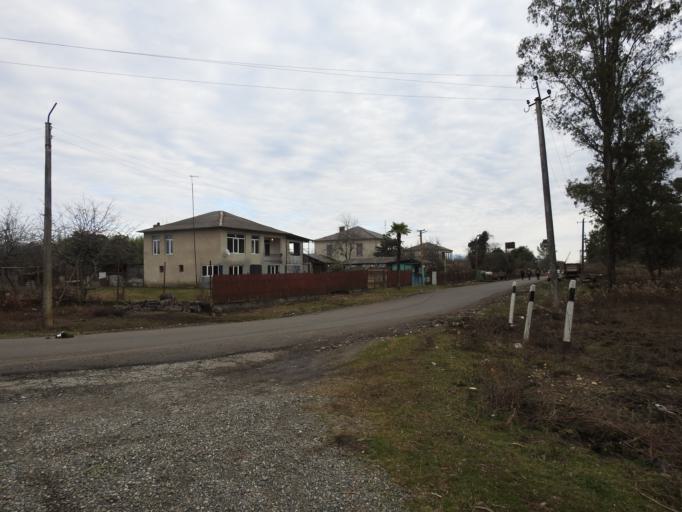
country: GE
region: Abkhazia
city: Dranda
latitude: 42.7950
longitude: 41.2607
